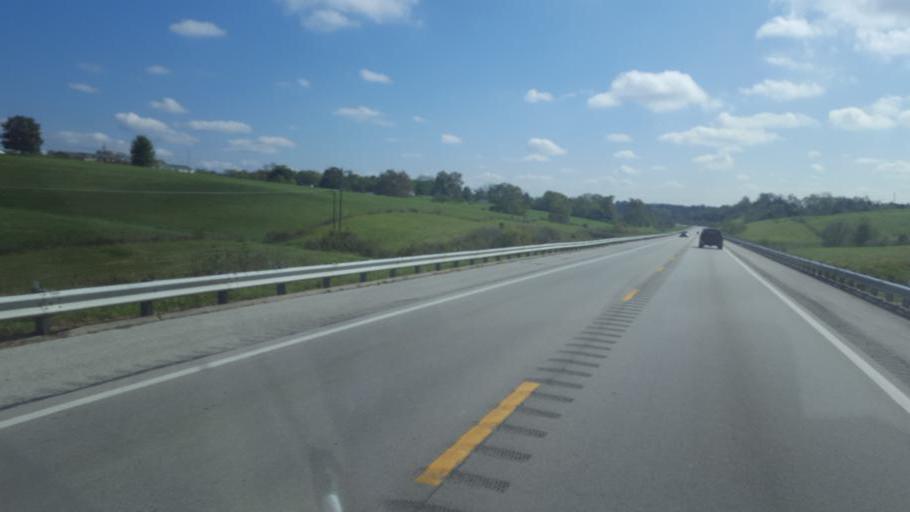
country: US
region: Kentucky
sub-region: Mason County
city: Maysville
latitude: 38.5900
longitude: -83.7091
